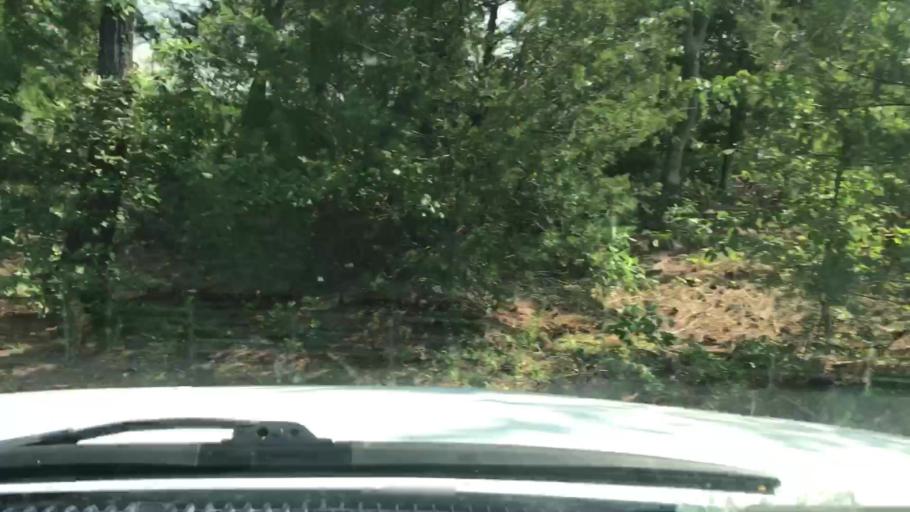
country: US
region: Virginia
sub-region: Henrico County
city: Tuckahoe
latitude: 37.5960
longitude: -77.6045
